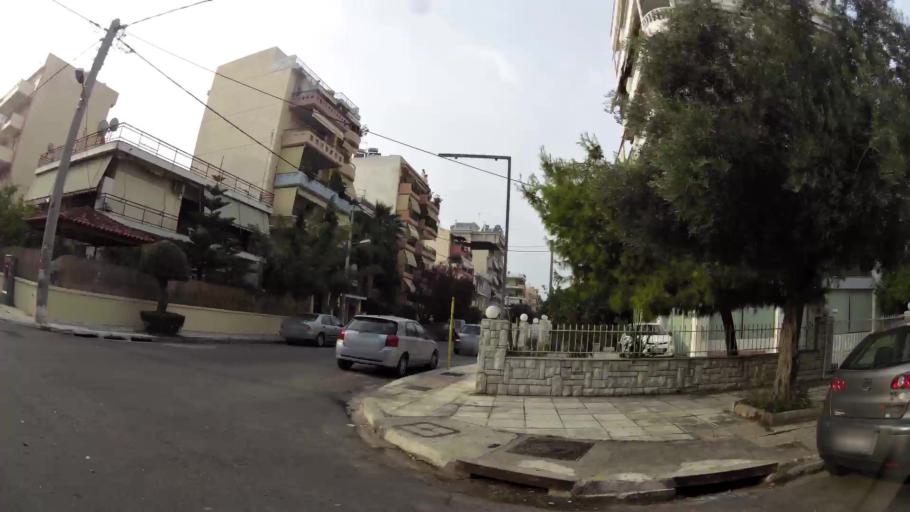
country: GR
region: Attica
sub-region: Nomarchia Athinas
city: Kallithea
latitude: 37.9457
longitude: 23.6924
